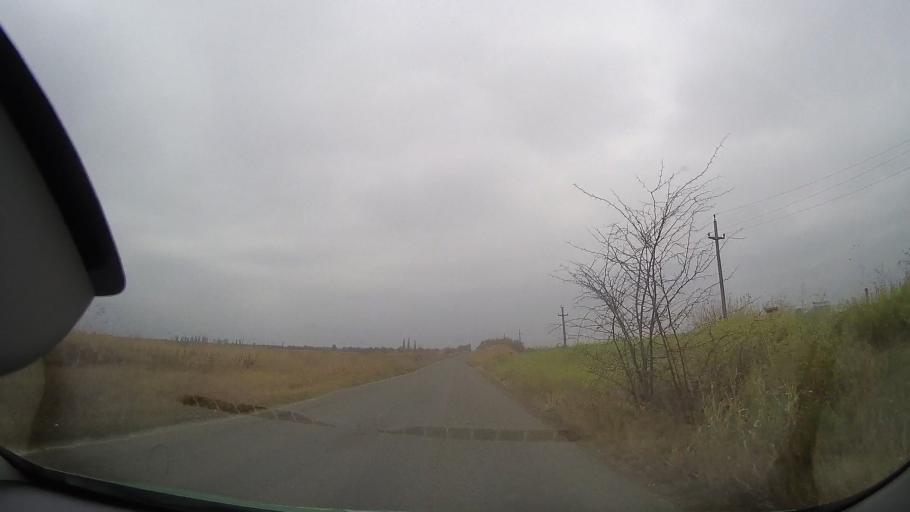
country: RO
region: Buzau
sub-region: Comuna Glodeanu-Silistea
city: Glodeanu-Silistea
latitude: 44.8158
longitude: 26.8449
